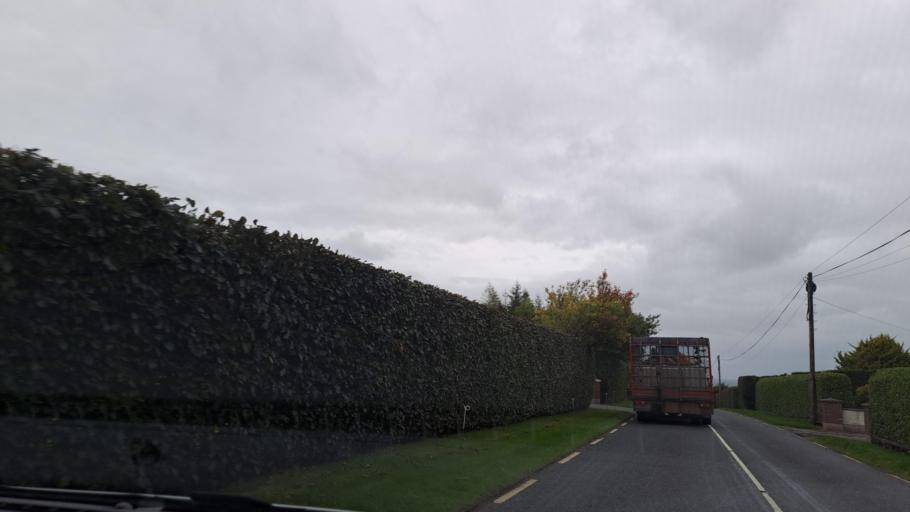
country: IE
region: Ulster
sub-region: County Monaghan
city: Castleblayney
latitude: 54.0885
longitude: -6.8309
